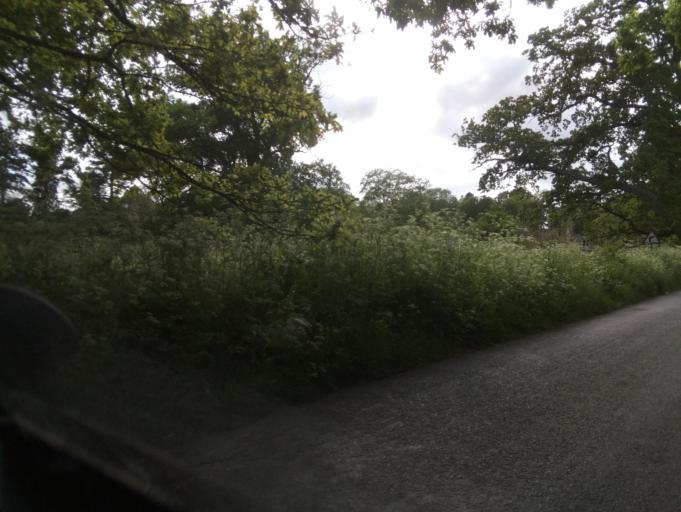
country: GB
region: England
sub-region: Gloucestershire
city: Moreton in Marsh
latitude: 52.0045
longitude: -1.7258
